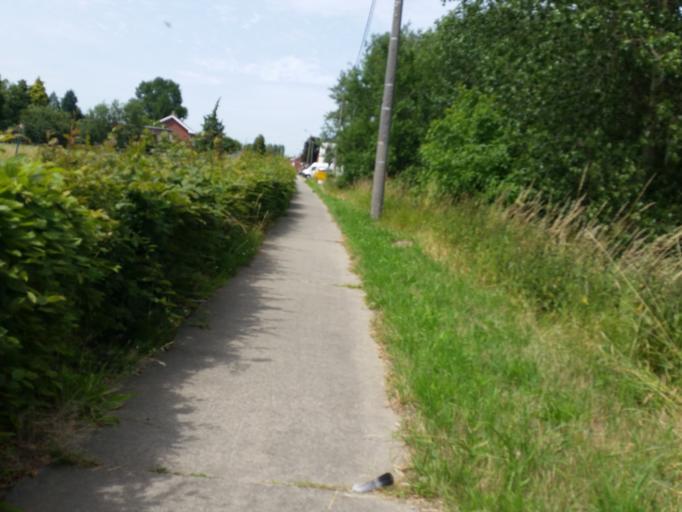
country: BE
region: Flanders
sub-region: Provincie Antwerpen
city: Rumst
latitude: 51.0388
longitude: 4.4161
